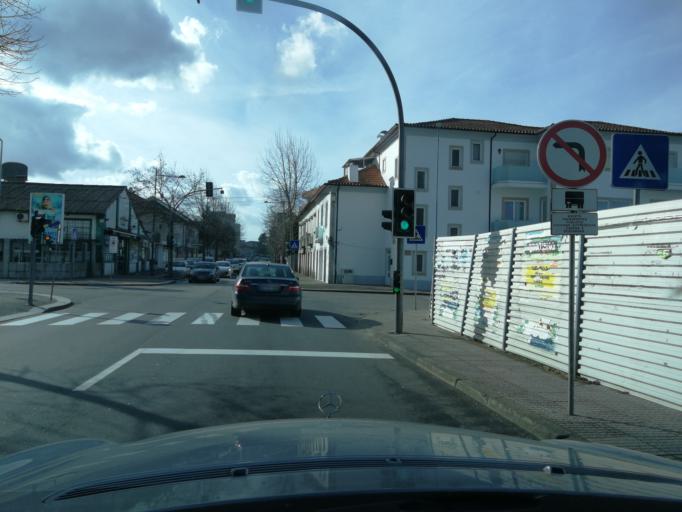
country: PT
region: Viana do Castelo
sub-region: Valenca
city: Valenza
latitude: 42.0276
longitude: -8.6381
